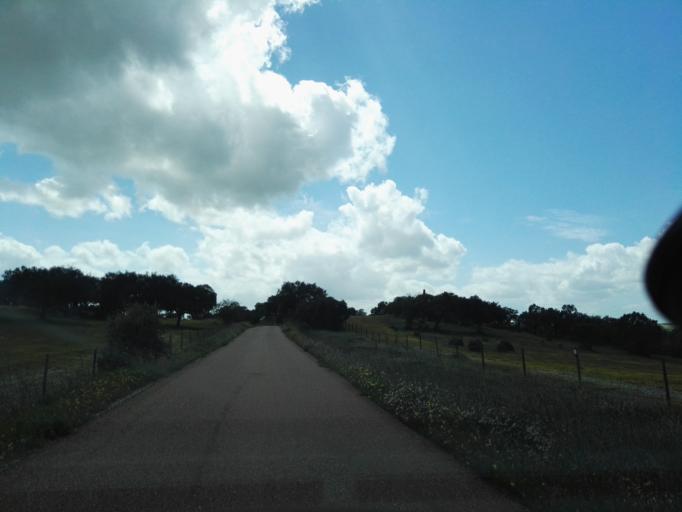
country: PT
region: Portalegre
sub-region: Elvas
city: Elvas
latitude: 38.9850
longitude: -7.1761
